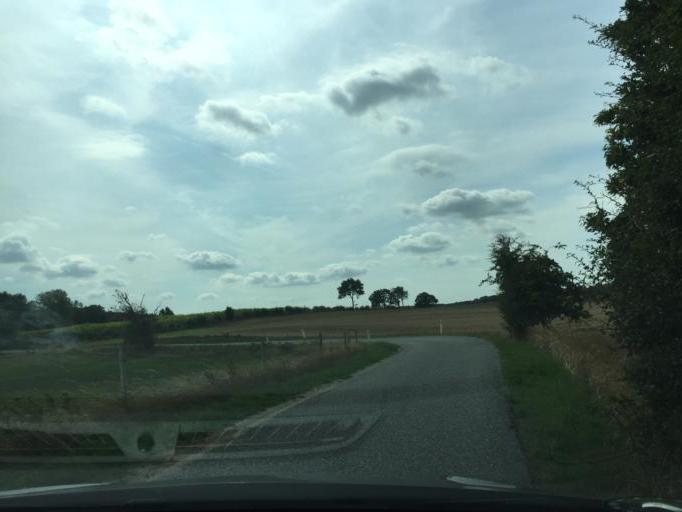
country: DK
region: South Denmark
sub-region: Nordfyns Kommune
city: Sonderso
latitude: 55.4106
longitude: 10.2263
